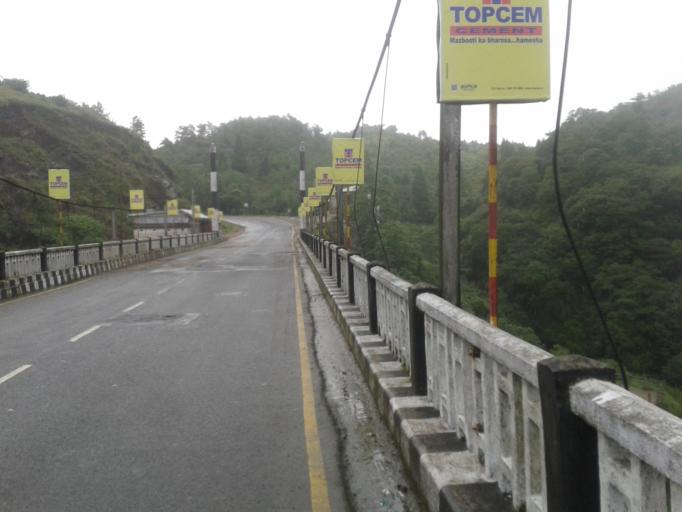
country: IN
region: Meghalaya
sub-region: East Khasi Hills
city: Cherrapunji
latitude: 25.4219
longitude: 91.7916
